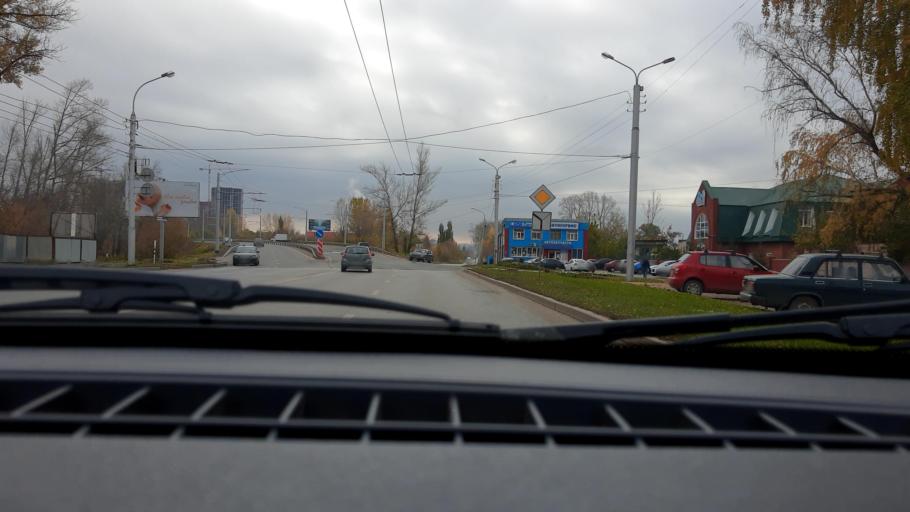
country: RU
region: Bashkortostan
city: Mikhaylovka
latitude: 54.7774
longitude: 55.8908
